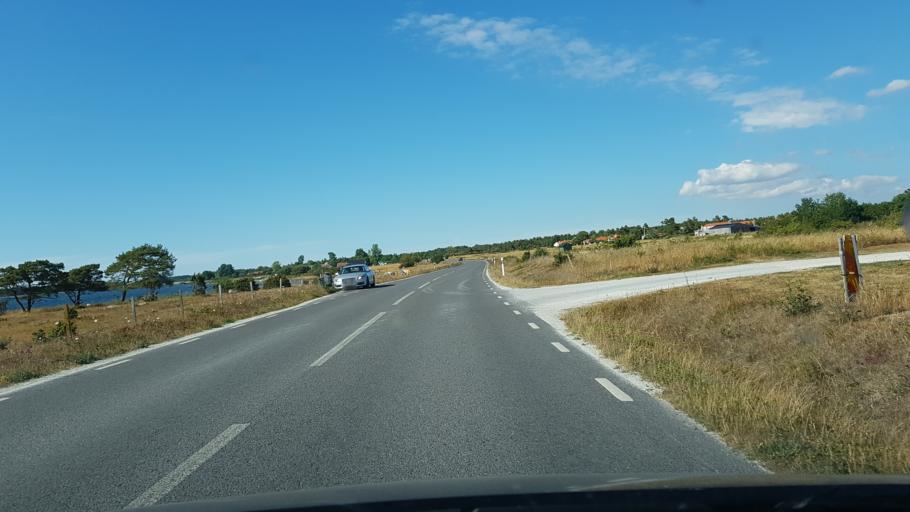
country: SE
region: Gotland
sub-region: Gotland
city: Klintehamn
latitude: 57.4240
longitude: 18.1490
